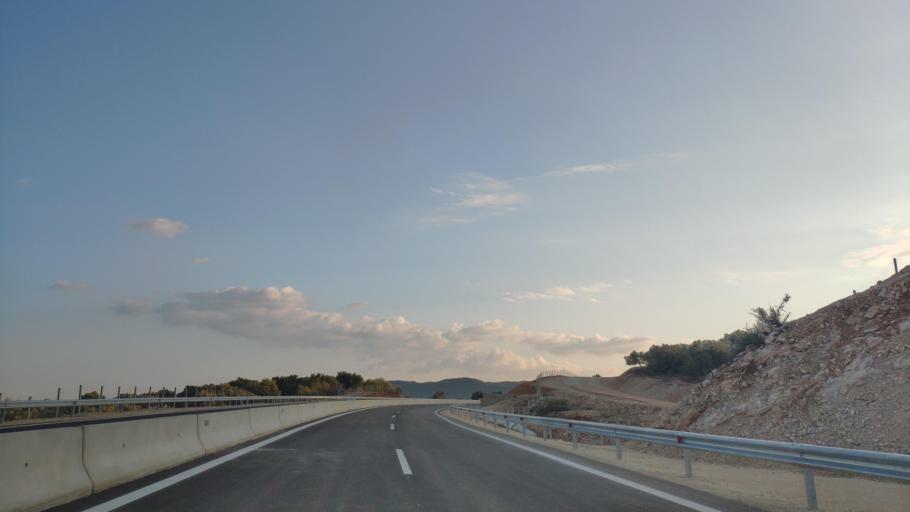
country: GR
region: West Greece
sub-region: Nomos Aitolias kai Akarnanias
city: Stanos
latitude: 38.7755
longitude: 21.1813
